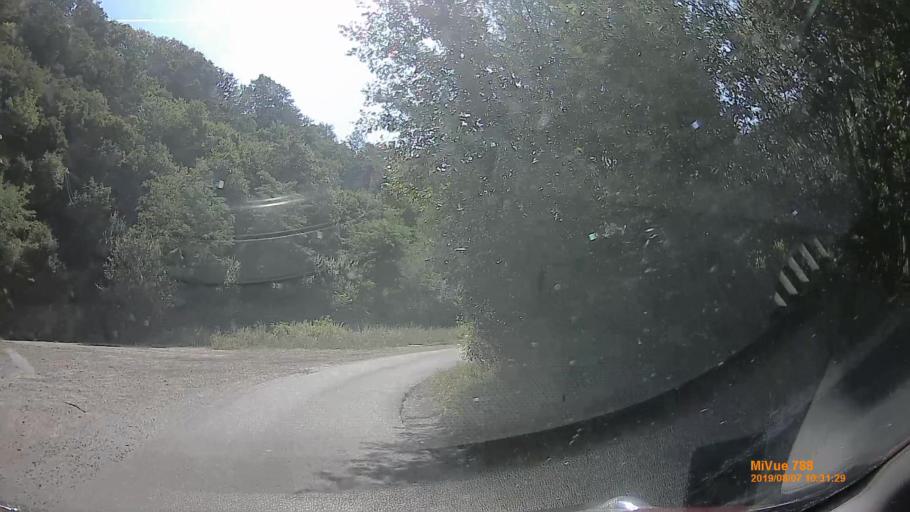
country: HU
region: Veszprem
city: Ajka
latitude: 47.0712
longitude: 17.5834
